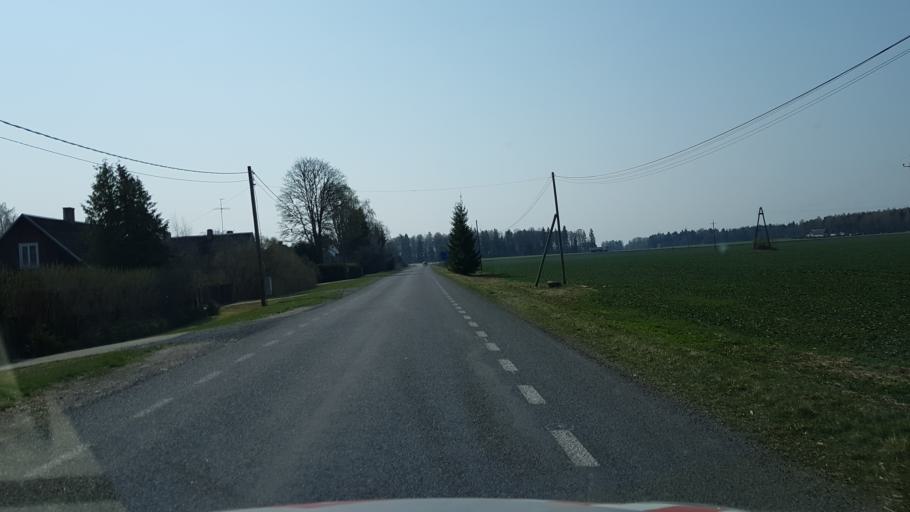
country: EE
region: Raplamaa
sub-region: Kehtna vald
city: Kehtna
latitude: 59.0598
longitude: 24.9531
